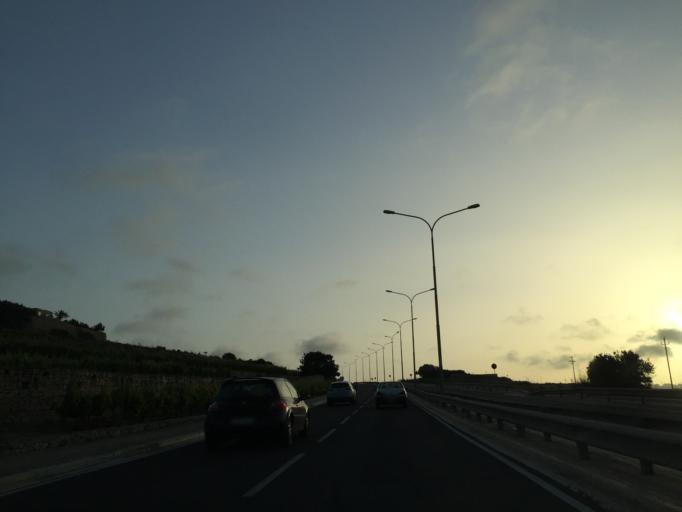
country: MT
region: Saint Paul's Bay
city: San Pawl il-Bahar
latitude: 35.9468
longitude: 14.3985
